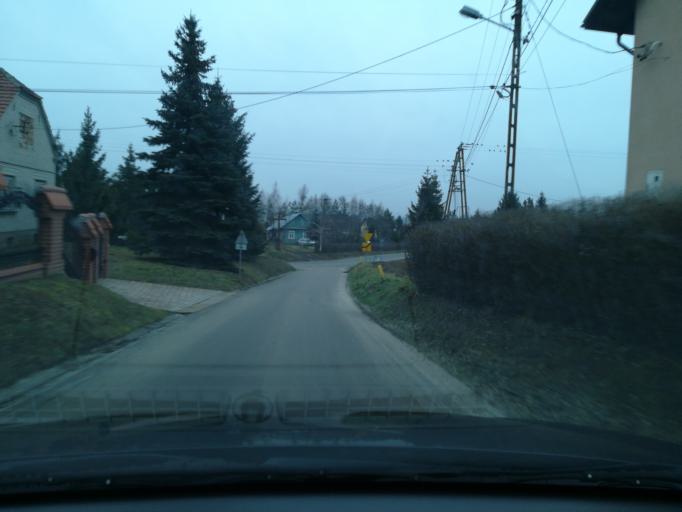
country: PL
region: Subcarpathian Voivodeship
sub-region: Powiat lancucki
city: Kosina
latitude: 50.0807
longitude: 22.3370
